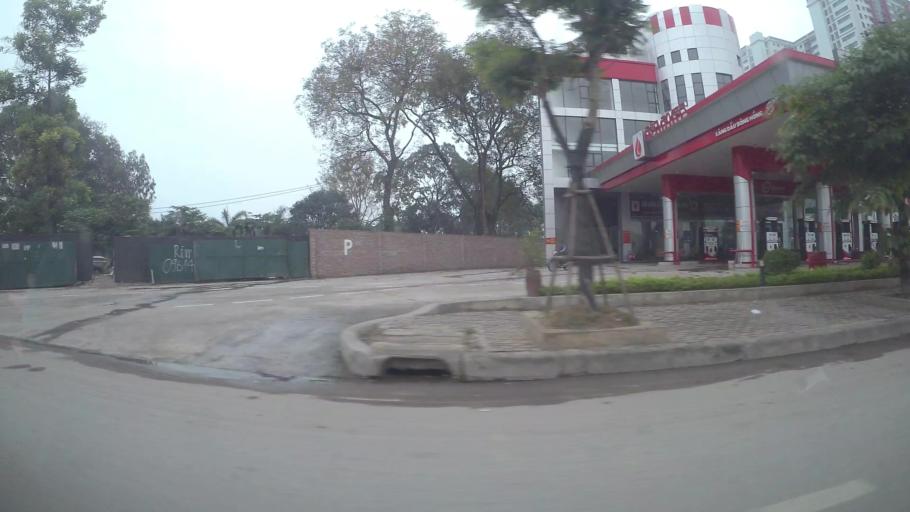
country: VN
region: Ha Noi
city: Van Dien
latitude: 20.9675
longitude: 105.8771
